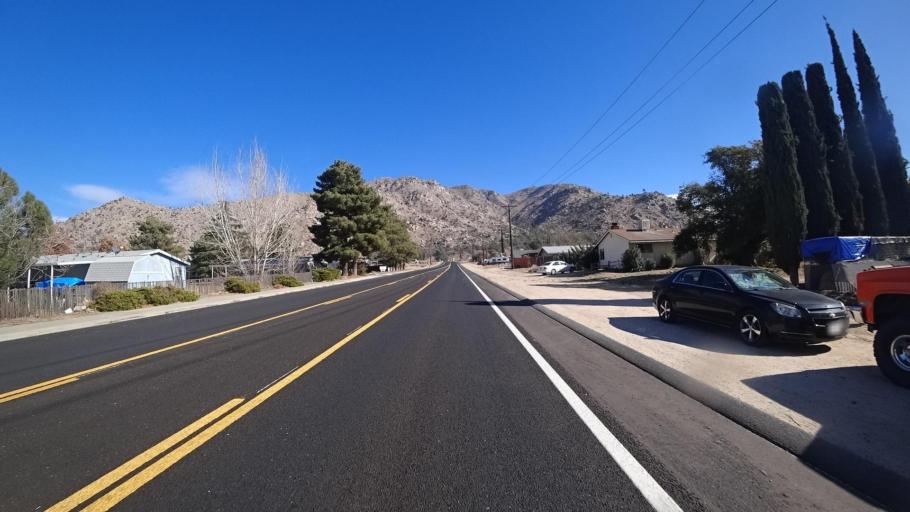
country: US
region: California
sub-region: Kern County
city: Lake Isabella
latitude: 35.6167
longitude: -118.4722
